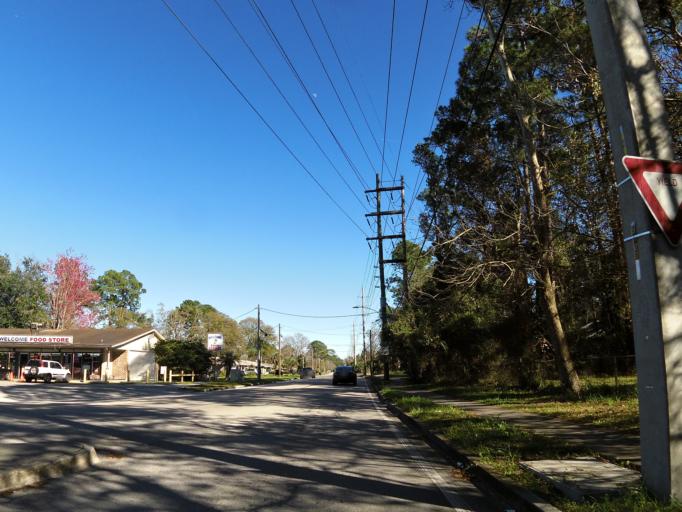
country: US
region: Florida
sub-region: Duval County
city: Jacksonville
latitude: 30.2846
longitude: -81.6112
